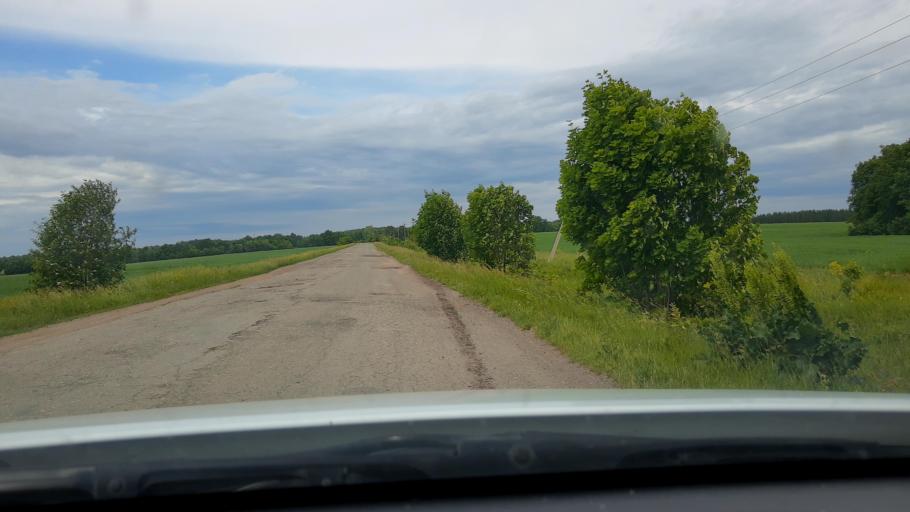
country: RU
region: Bashkortostan
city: Iglino
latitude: 54.7544
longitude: 56.5302
